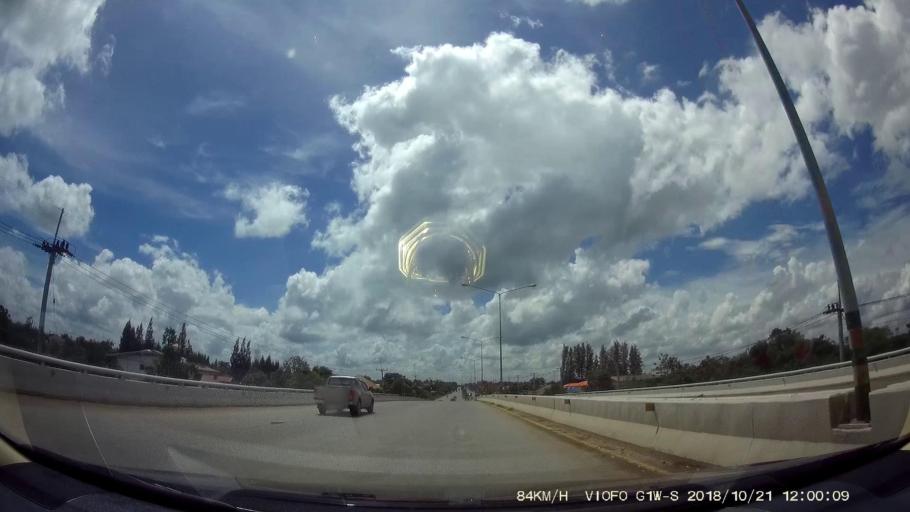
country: TH
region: Chaiyaphum
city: Chatturat
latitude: 15.5548
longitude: 101.8447
